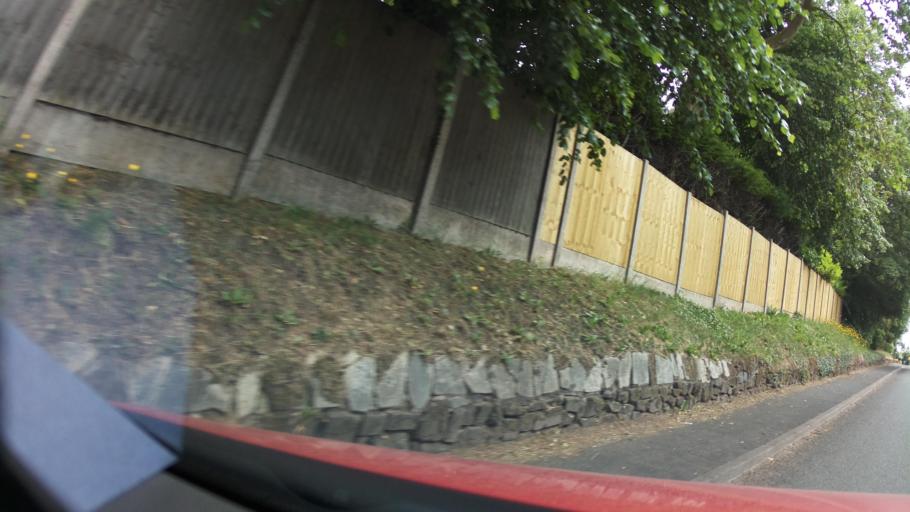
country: GB
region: England
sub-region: Staffordshire
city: Stafford
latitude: 52.7949
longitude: -2.1182
